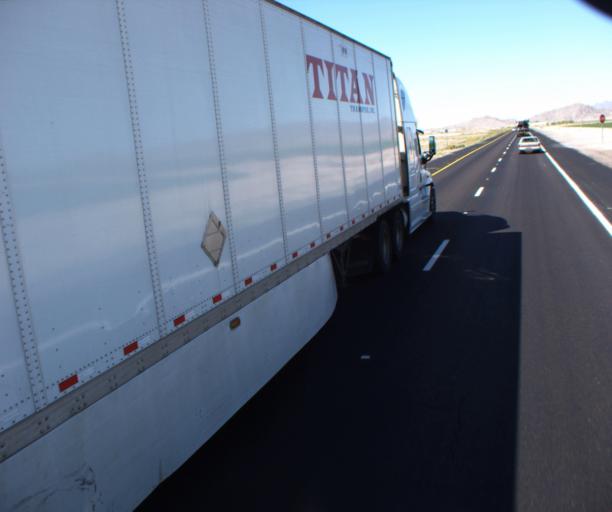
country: US
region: Arizona
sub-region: Maricopa County
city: Buckeye
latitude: 33.3841
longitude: -112.6253
